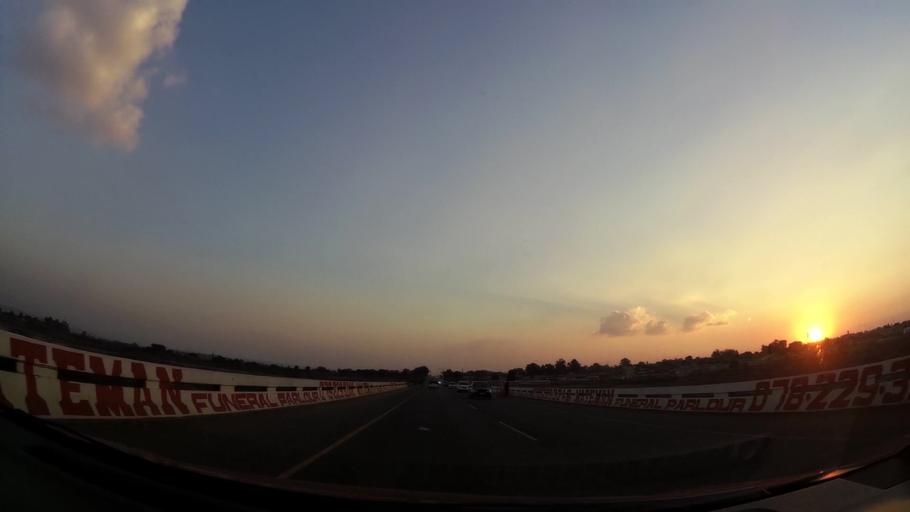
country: ZA
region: Gauteng
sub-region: City of Johannesburg Metropolitan Municipality
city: Soweto
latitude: -26.2899
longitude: 27.8858
